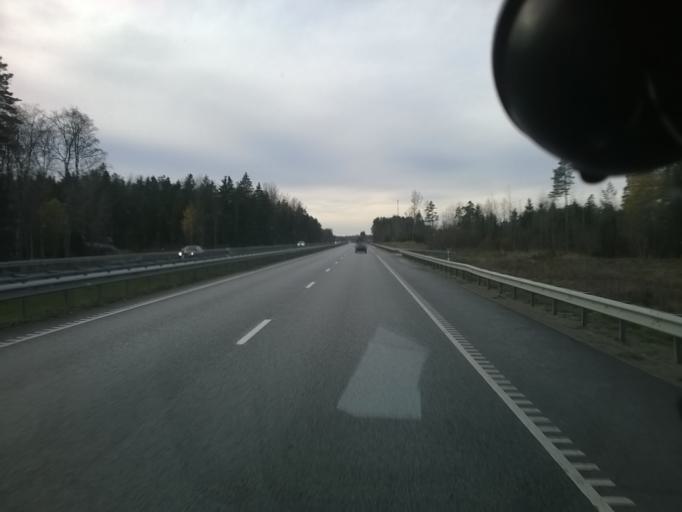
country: EE
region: Harju
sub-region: Kiili vald
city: Kiili
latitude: 59.3307
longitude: 24.7921
